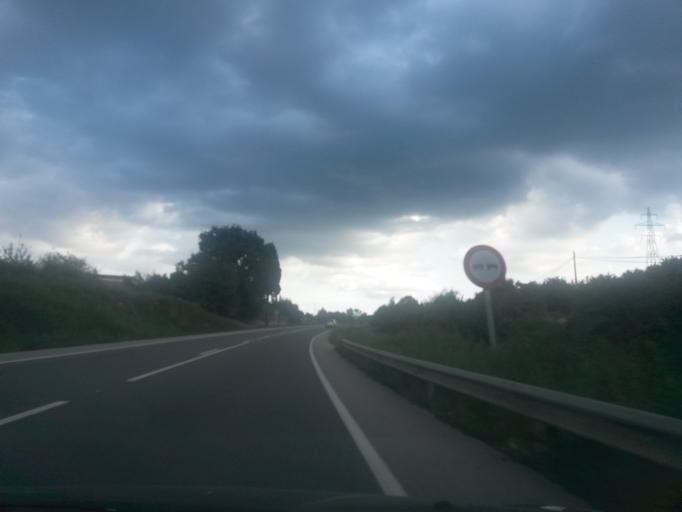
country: ES
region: Catalonia
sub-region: Provincia de Girona
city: Angles
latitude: 41.9301
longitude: 2.6486
